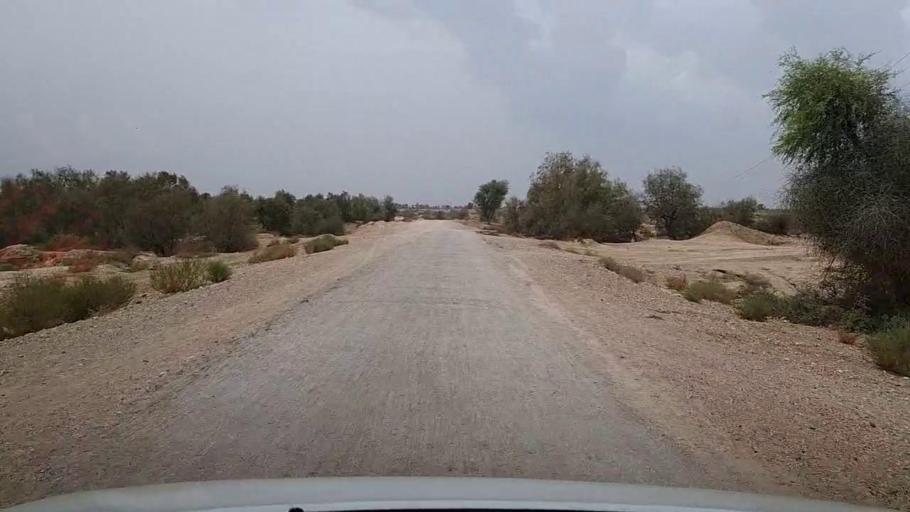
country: PK
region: Sindh
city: Sehwan
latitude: 26.3157
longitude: 67.7484
